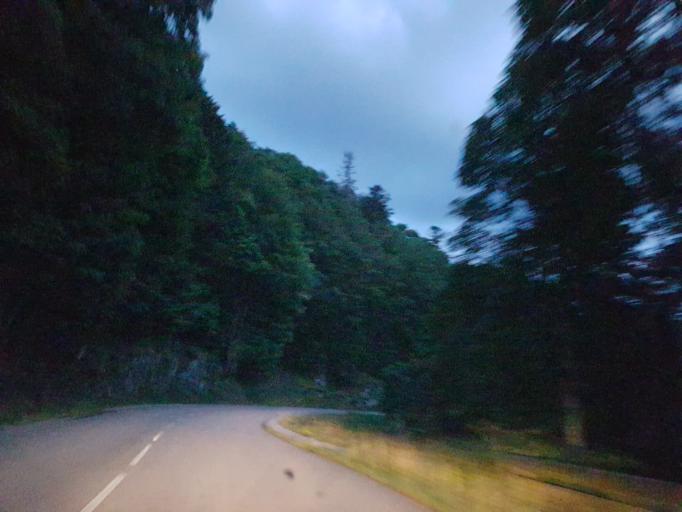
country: FR
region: Lorraine
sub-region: Departement des Vosges
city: Xonrupt-Longemer
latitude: 48.0549
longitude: 6.9974
